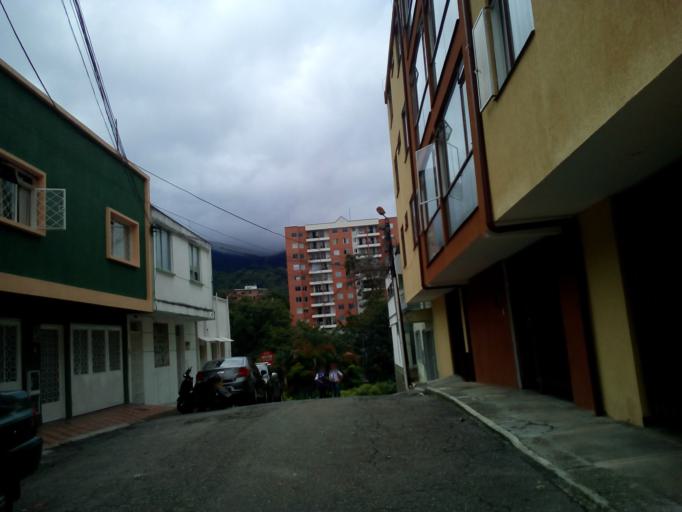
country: CO
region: Tolima
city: Ibague
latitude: 4.4468
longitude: -75.2432
